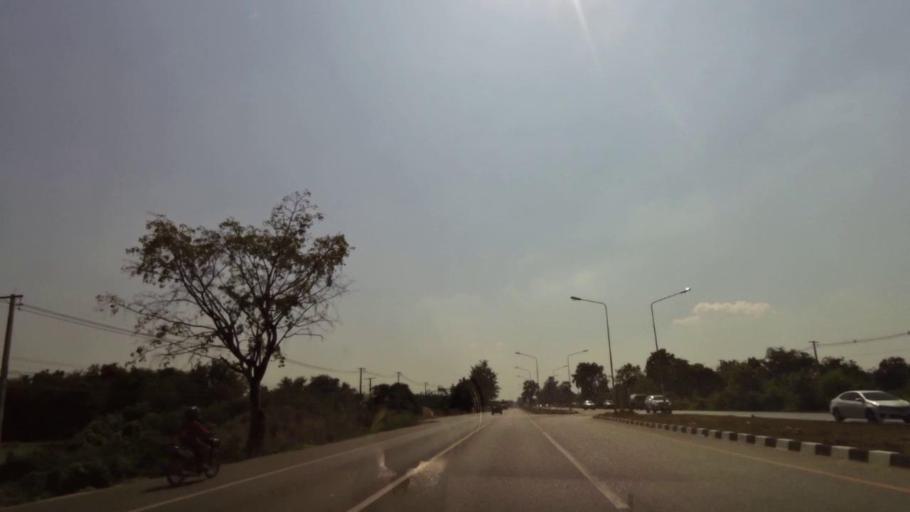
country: TH
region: Phichit
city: Bueng Na Rang
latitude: 16.2648
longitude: 100.1263
